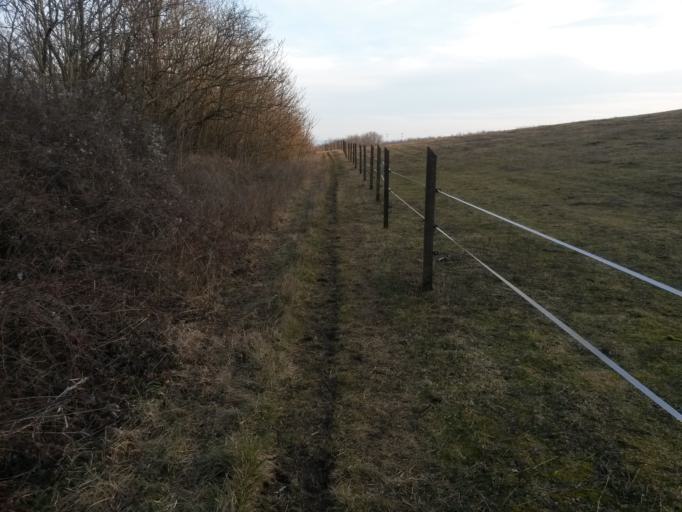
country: HU
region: Pest
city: Perbal
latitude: 47.5953
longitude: 18.7297
